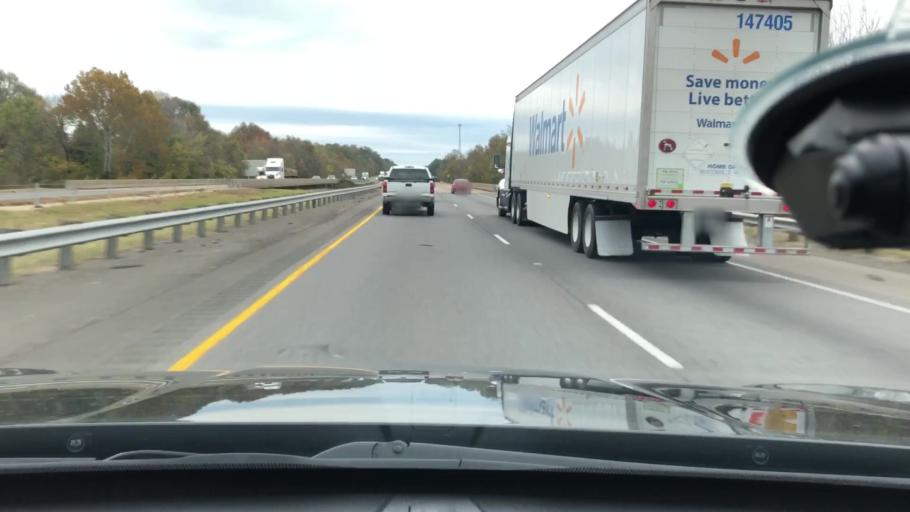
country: US
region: Arkansas
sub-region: Clark County
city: Gurdon
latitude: 34.0097
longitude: -93.1706
